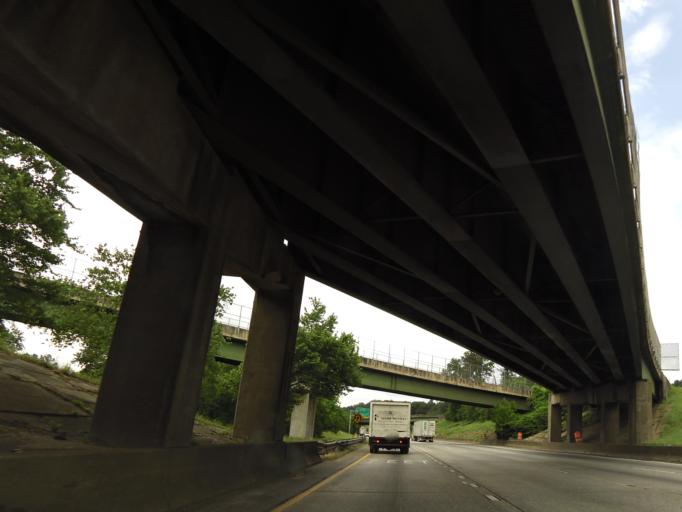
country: US
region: Georgia
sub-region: Fulton County
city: East Point
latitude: 33.7603
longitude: -84.4929
